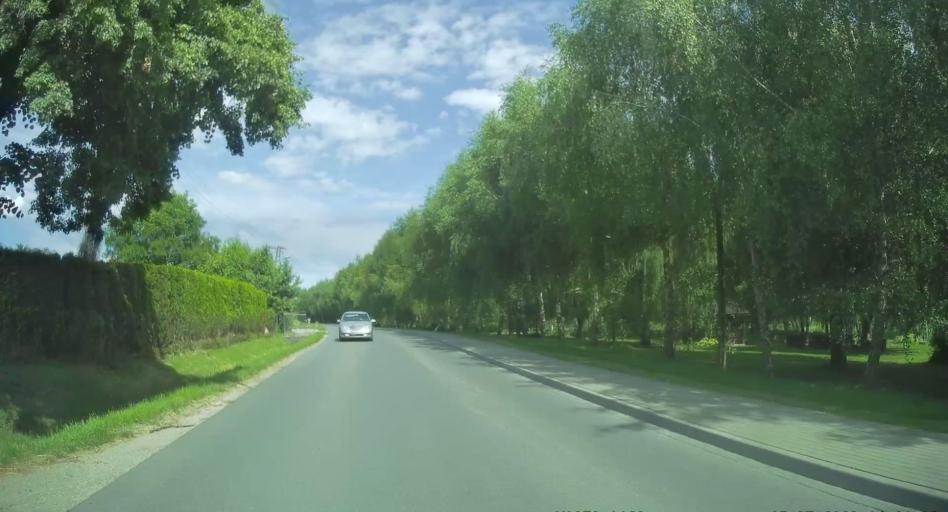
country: PL
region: Subcarpathian Voivodeship
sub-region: Powiat przemyski
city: Zurawica
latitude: 49.8067
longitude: 22.8206
